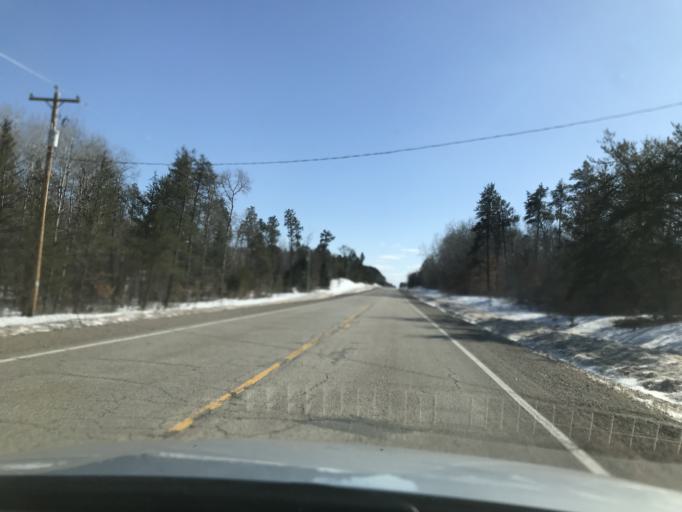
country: US
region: Wisconsin
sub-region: Marinette County
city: Peshtigo
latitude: 45.3312
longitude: -88.1019
